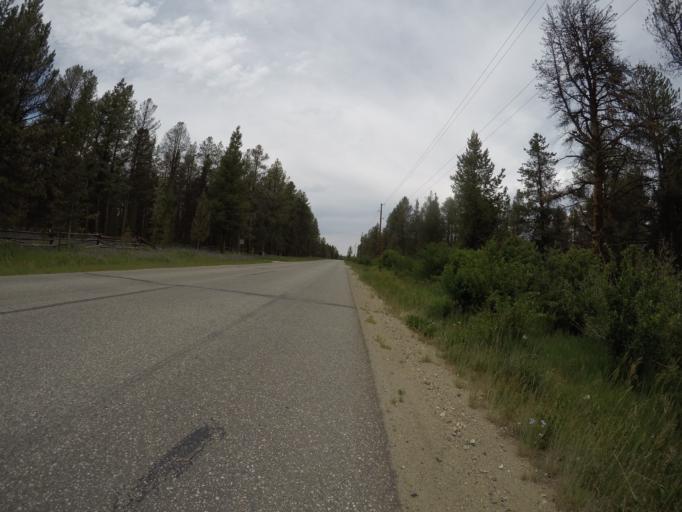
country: US
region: Colorado
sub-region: Grand County
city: Fraser
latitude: 39.9677
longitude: -105.8563
